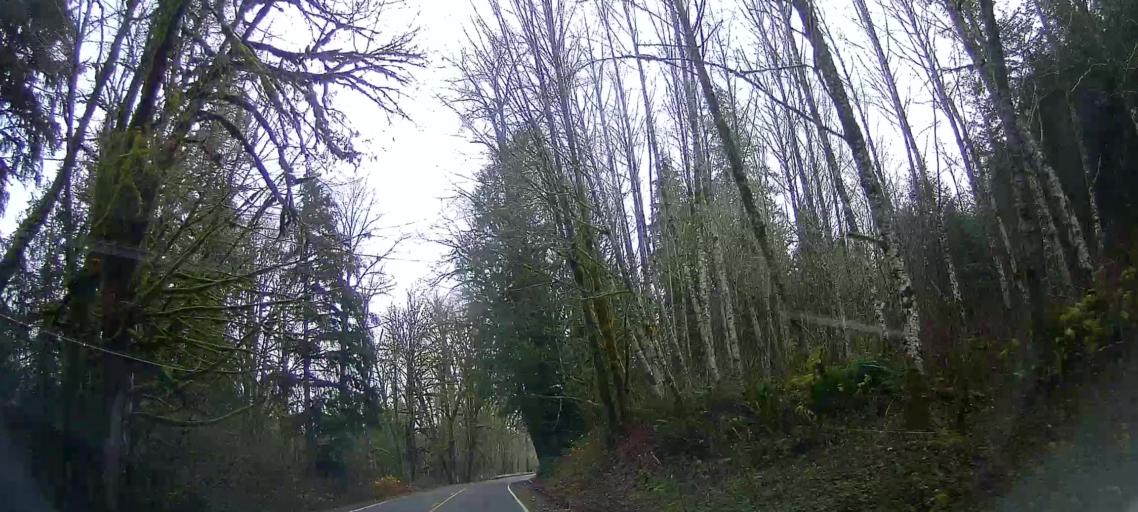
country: US
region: Washington
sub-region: Skagit County
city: Sedro-Woolley
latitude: 48.5117
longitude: -121.8835
